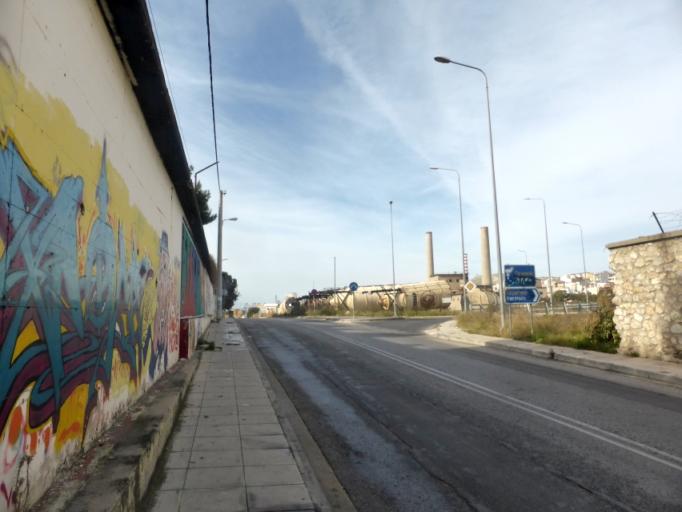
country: GR
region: Attica
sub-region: Nomos Piraios
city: Drapetsona
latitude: 37.9467
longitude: 23.6216
